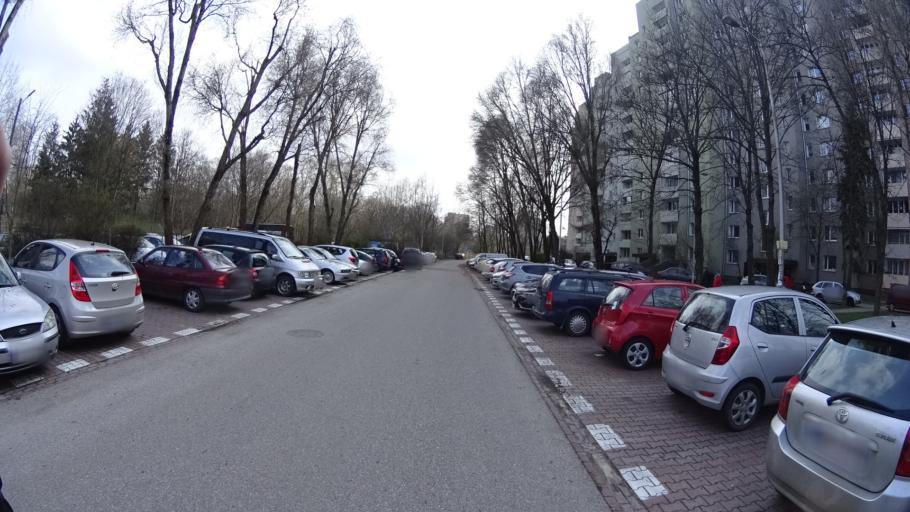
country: PL
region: Masovian Voivodeship
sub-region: Warszawa
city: Bemowo
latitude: 52.2291
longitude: 20.9195
